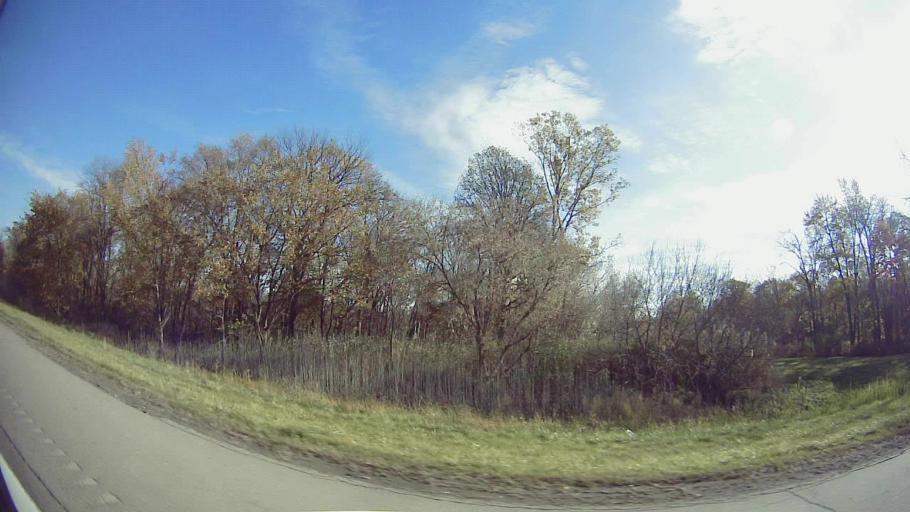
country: US
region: Michigan
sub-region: Wayne County
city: Romulus
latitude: 42.2465
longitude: -83.4397
